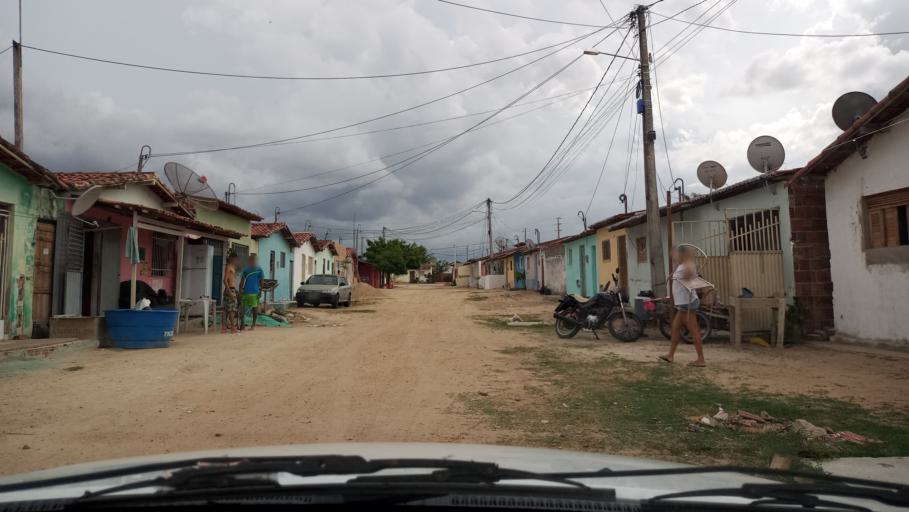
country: BR
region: Rio Grande do Norte
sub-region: Tangara
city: Tangara
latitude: -6.1908
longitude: -35.8013
